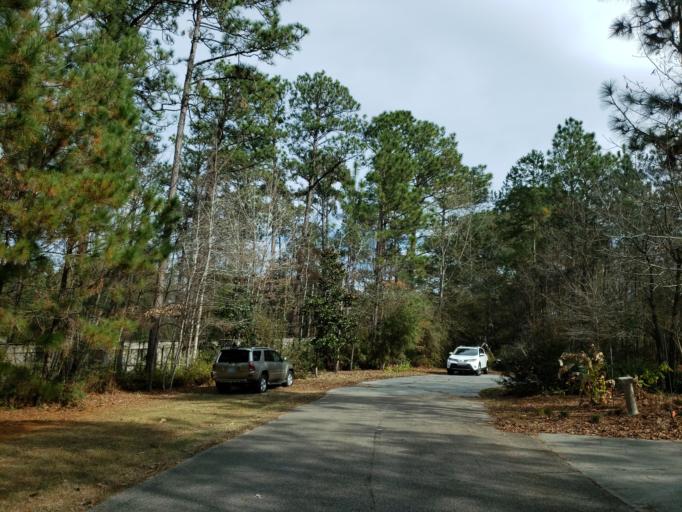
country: US
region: Mississippi
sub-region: Lamar County
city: West Hattiesburg
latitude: 31.3028
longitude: -89.3454
